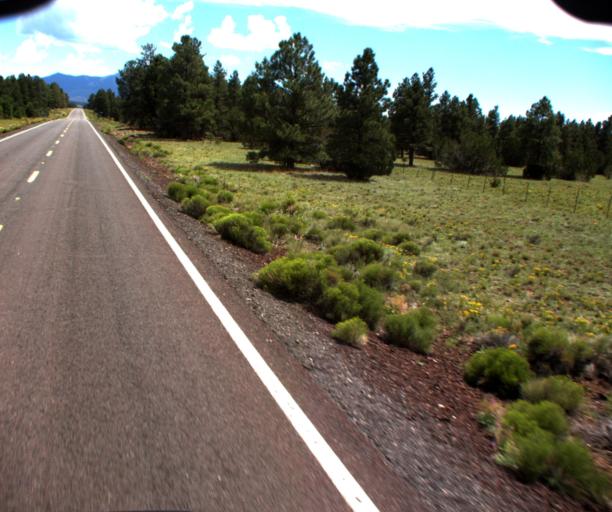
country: US
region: Arizona
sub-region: Coconino County
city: Parks
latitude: 35.4820
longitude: -111.8015
